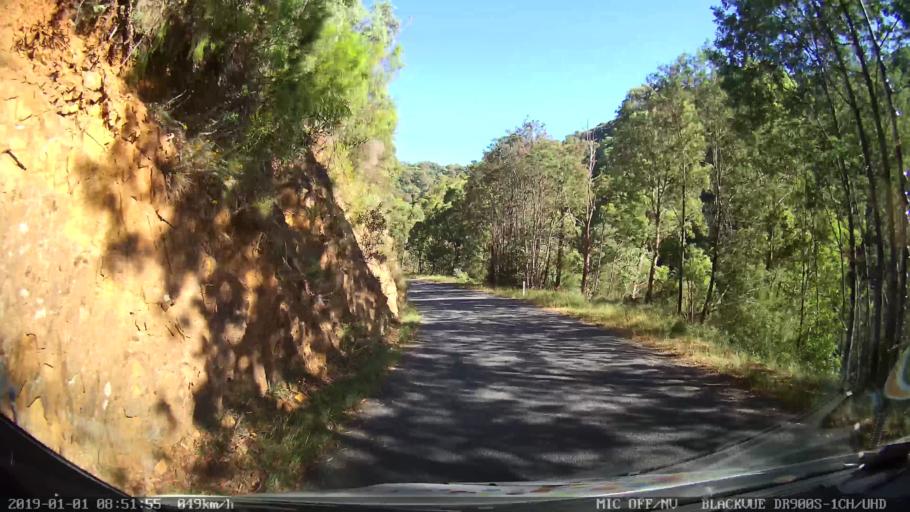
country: AU
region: New South Wales
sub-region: Snowy River
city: Jindabyne
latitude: -36.2684
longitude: 148.2010
